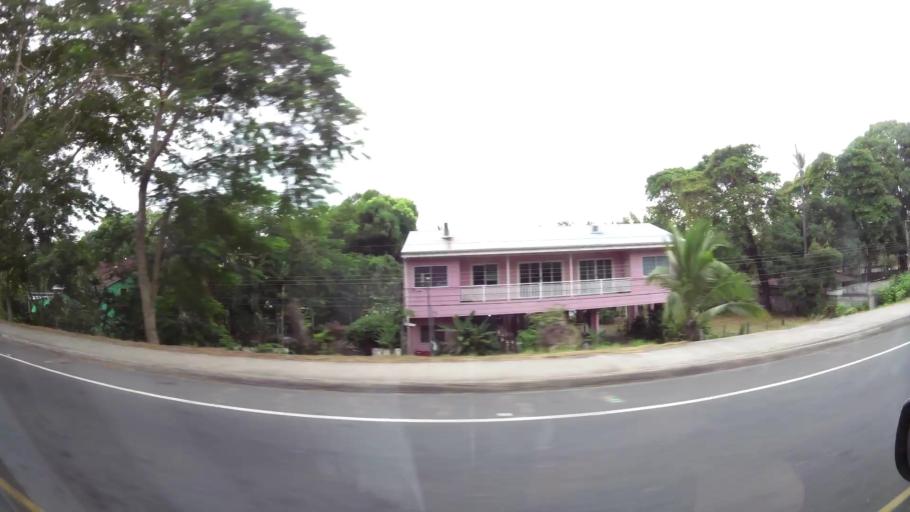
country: CR
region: Puntarenas
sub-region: Canton Central de Puntarenas
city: Chacarita
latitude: 9.9622
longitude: -84.7362
